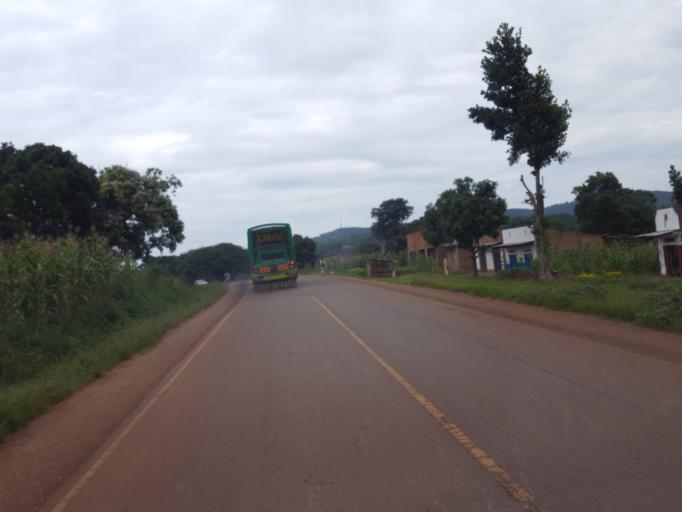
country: UG
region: Central Region
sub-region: Mityana District
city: Mityana
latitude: 0.6707
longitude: 32.0867
